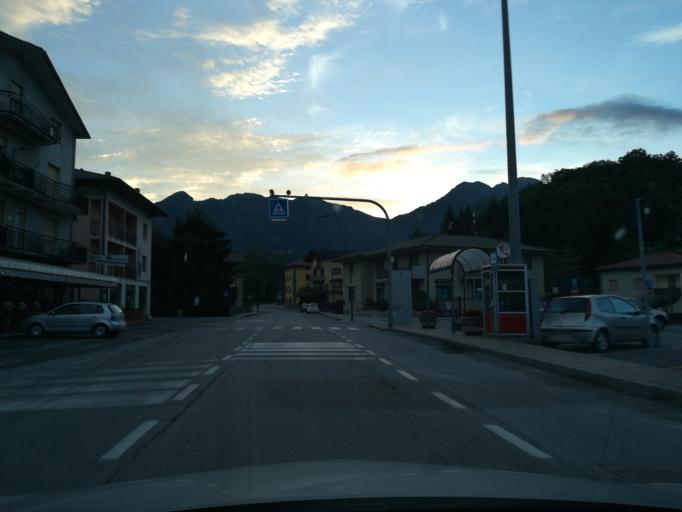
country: IT
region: Lombardy
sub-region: Provincia di Bergamo
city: Selino Basso
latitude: 45.8151
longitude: 9.5318
